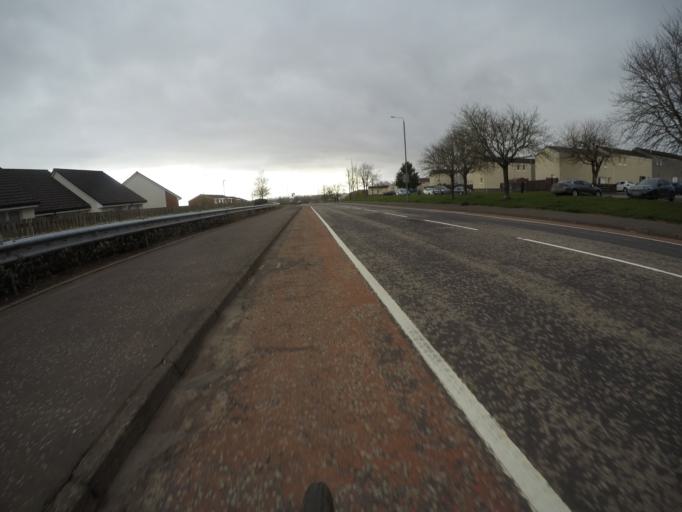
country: GB
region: Scotland
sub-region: East Ayrshire
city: Kilmarnock
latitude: 55.6216
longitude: -4.4710
